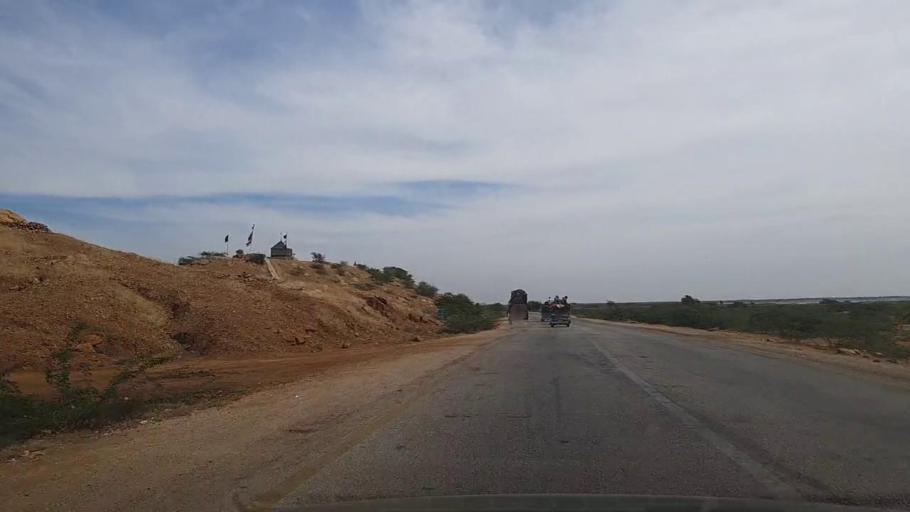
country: PK
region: Sindh
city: Daro Mehar
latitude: 24.8797
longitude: 68.0509
